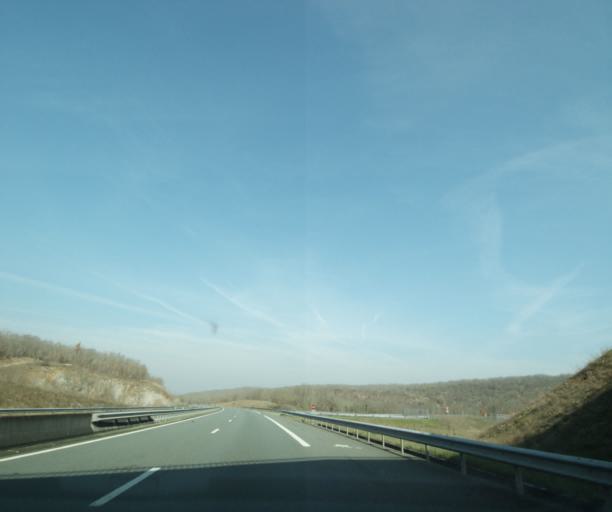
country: FR
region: Midi-Pyrenees
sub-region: Departement du Lot
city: Le Vigan
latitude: 44.7872
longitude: 1.5286
